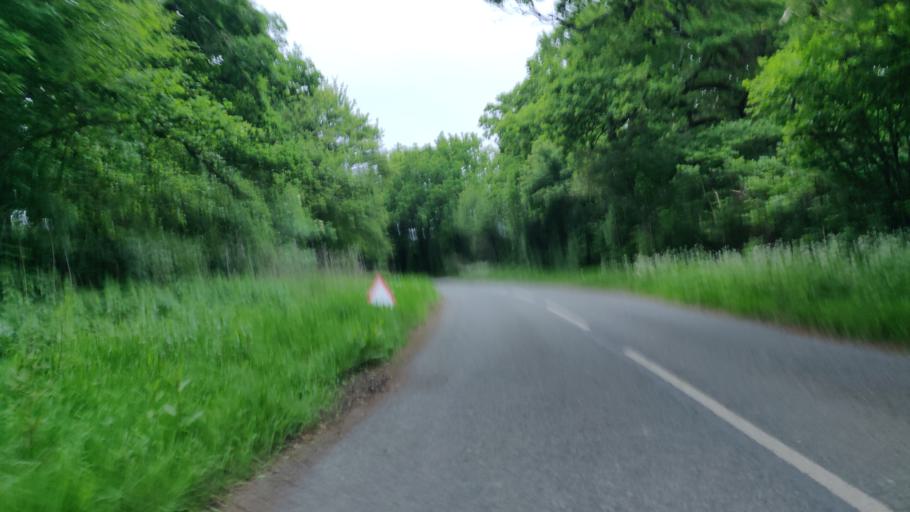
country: GB
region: England
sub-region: West Sussex
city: Partridge Green
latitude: 50.9843
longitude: -0.2999
